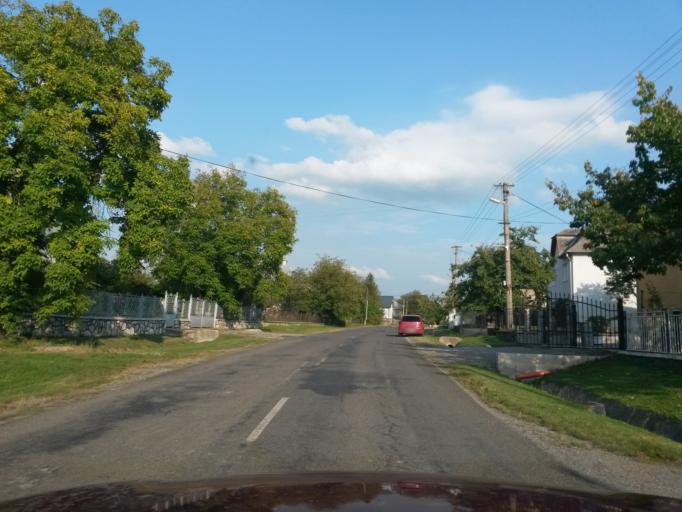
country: SK
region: Kosicky
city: Kosice
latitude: 48.7671
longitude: 21.4349
